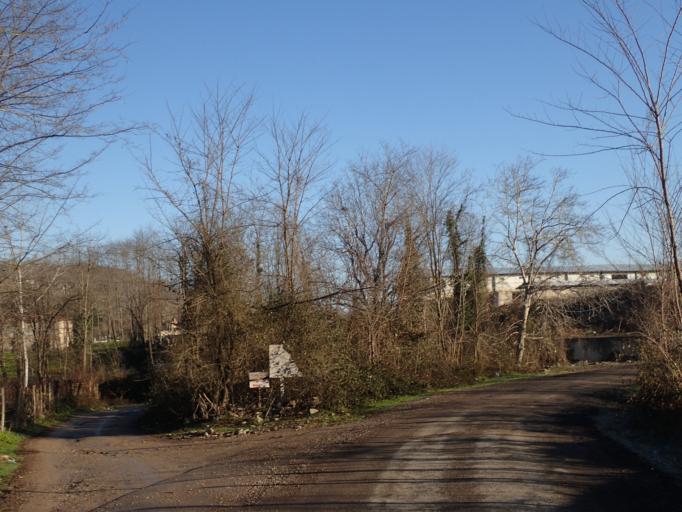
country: TR
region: Ordu
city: Camas
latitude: 40.9465
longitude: 37.5012
